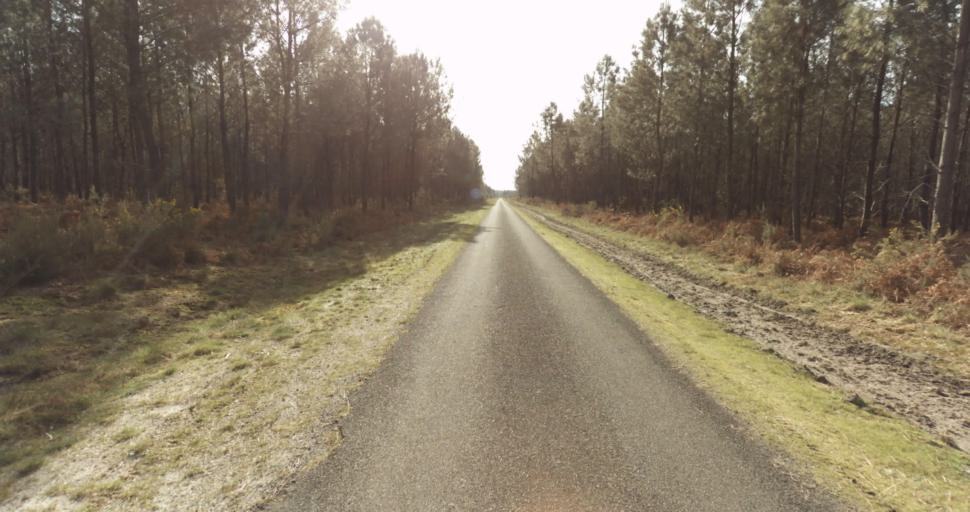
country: FR
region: Aquitaine
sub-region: Departement des Landes
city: Roquefort
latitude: 44.1290
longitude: -0.3147
